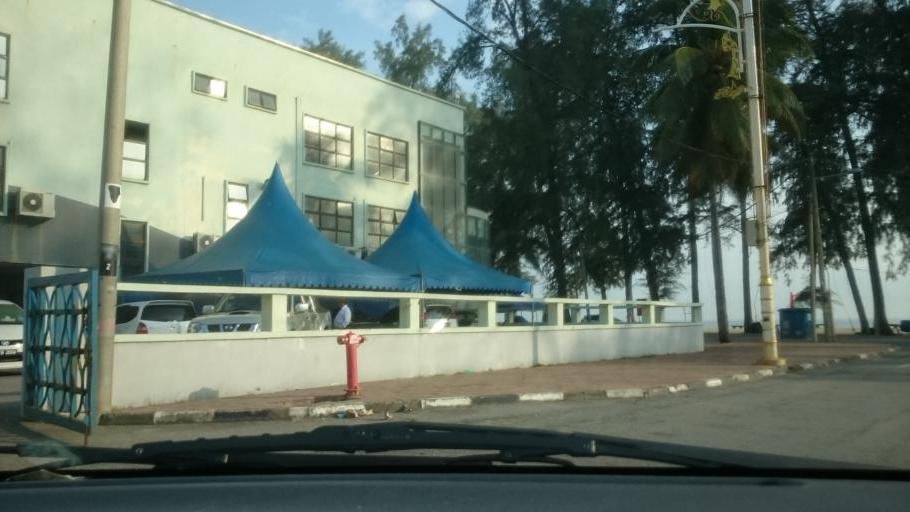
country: MY
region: Terengganu
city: Kuala Terengganu
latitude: 5.3243
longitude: 103.1537
